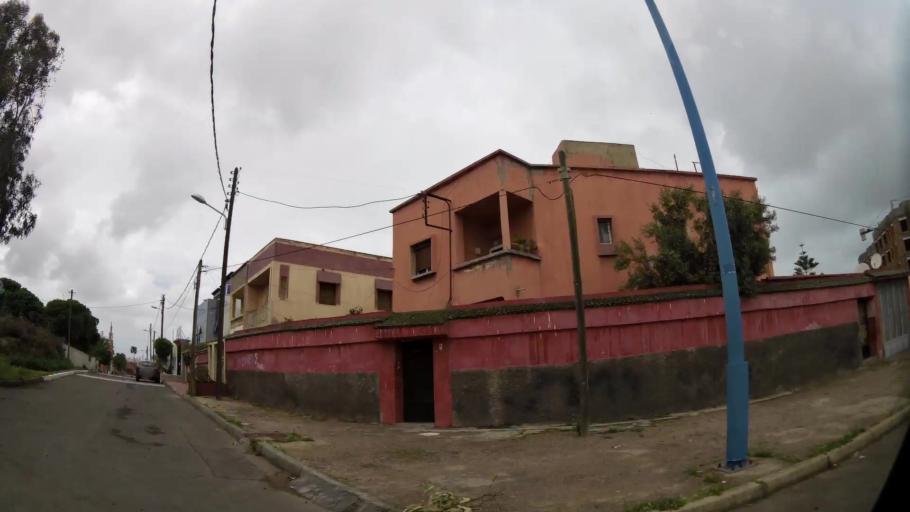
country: MA
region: Grand Casablanca
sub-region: Mediouna
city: Tit Mellil
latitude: 33.6134
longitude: -7.5247
